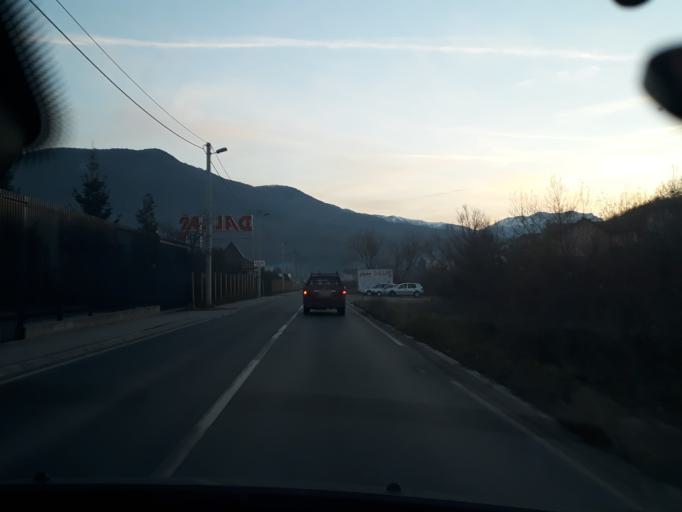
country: BA
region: Federation of Bosnia and Herzegovina
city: Hadzici
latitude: 43.8555
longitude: 18.2497
